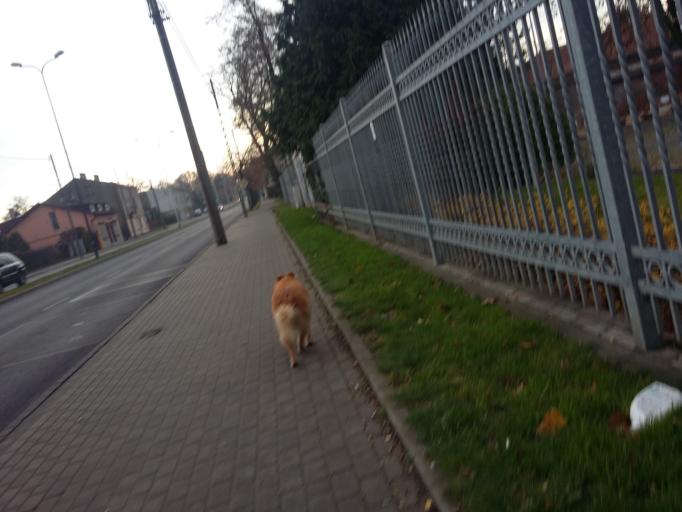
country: PL
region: Lodz Voivodeship
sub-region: Powiat pabianicki
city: Ksawerow
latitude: 51.7096
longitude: 19.4298
